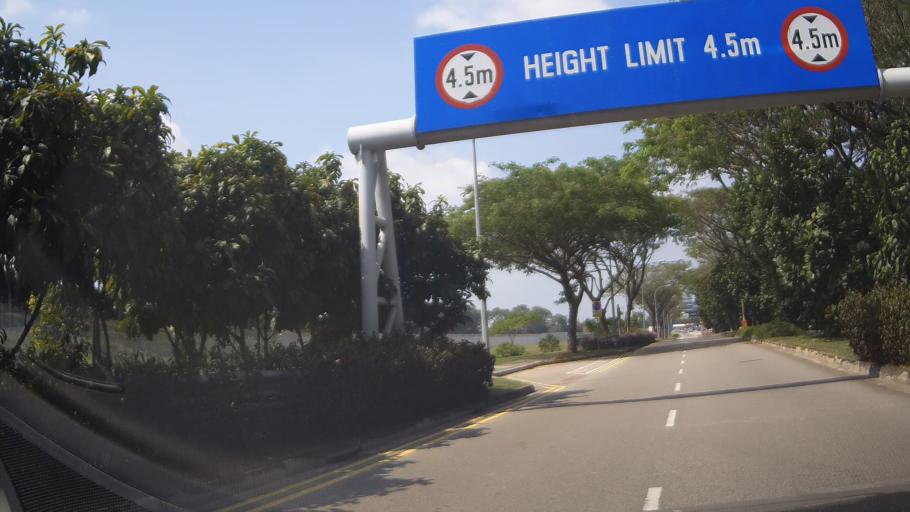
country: SG
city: Singapore
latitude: 1.3623
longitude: 103.9052
